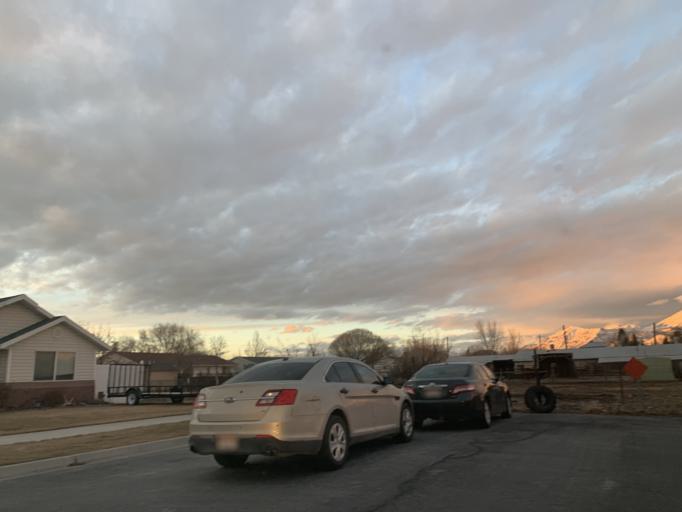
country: US
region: Utah
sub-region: Utah County
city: Provo
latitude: 40.2397
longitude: -111.7033
